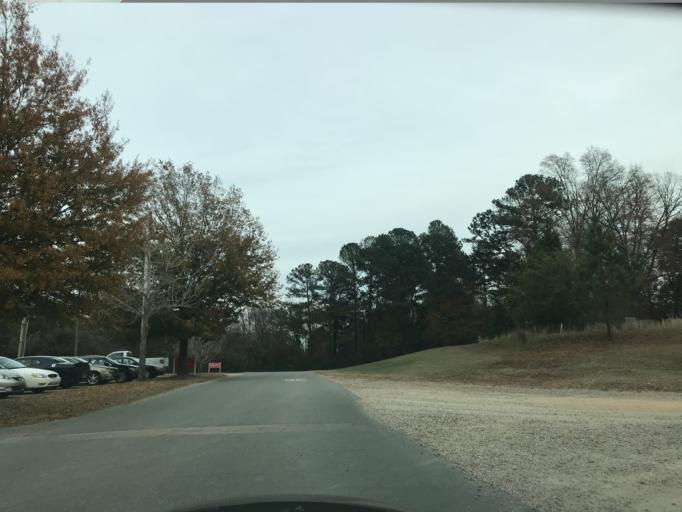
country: US
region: North Carolina
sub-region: Wake County
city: West Raleigh
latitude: 35.7890
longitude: -78.6990
